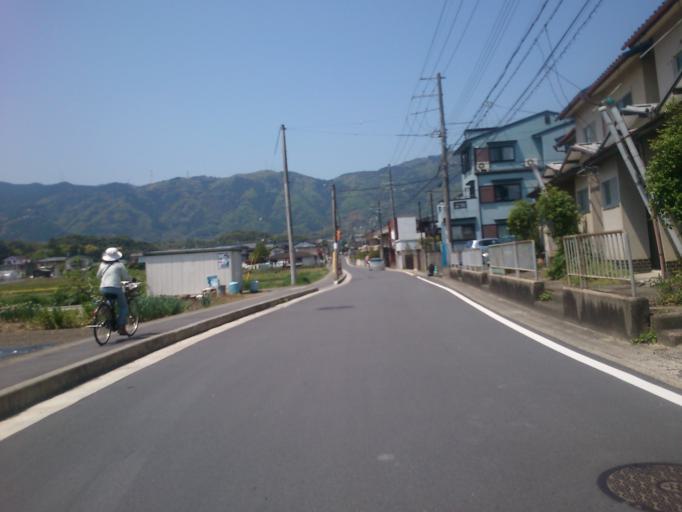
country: JP
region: Kyoto
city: Muko
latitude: 34.9529
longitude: 135.6707
